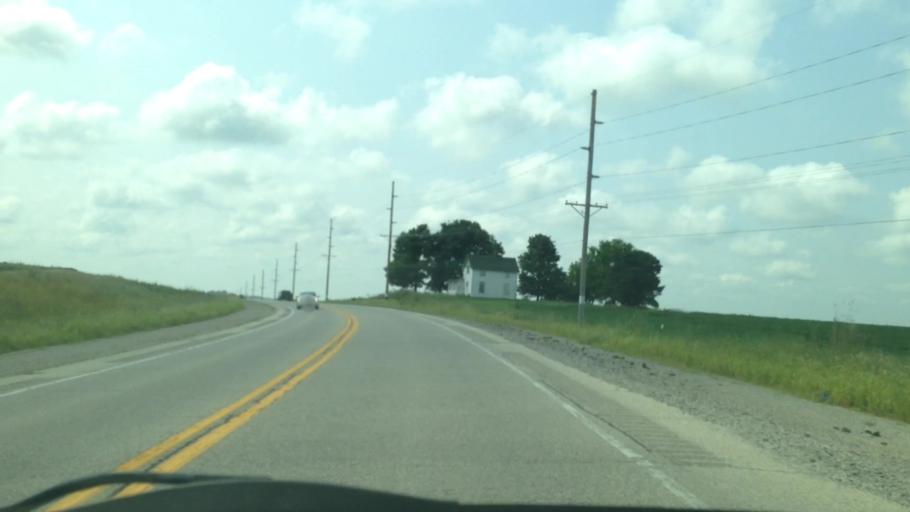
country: US
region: Iowa
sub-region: Benton County
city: Walford
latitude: 41.8728
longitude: -91.8701
